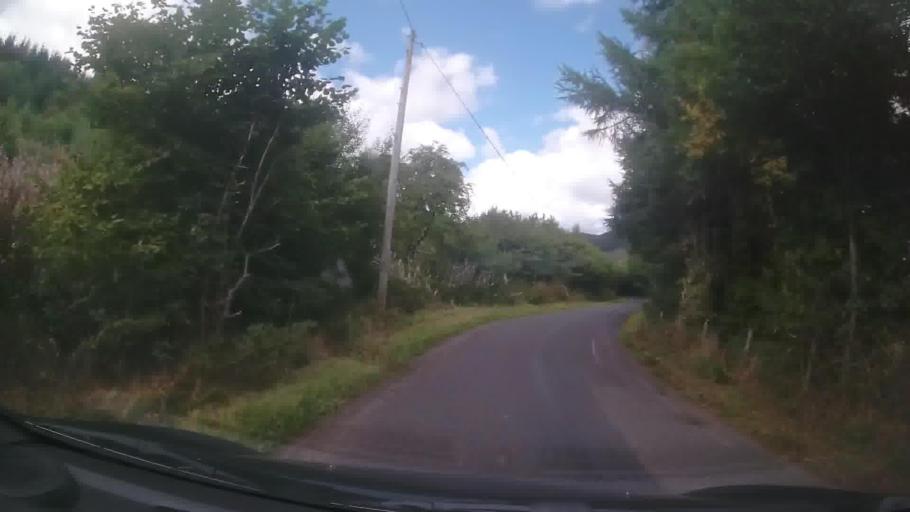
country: GB
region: Wales
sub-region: Merthyr Tydfil County Borough
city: Merthyr Tydfil
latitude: 51.8161
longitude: -3.3744
